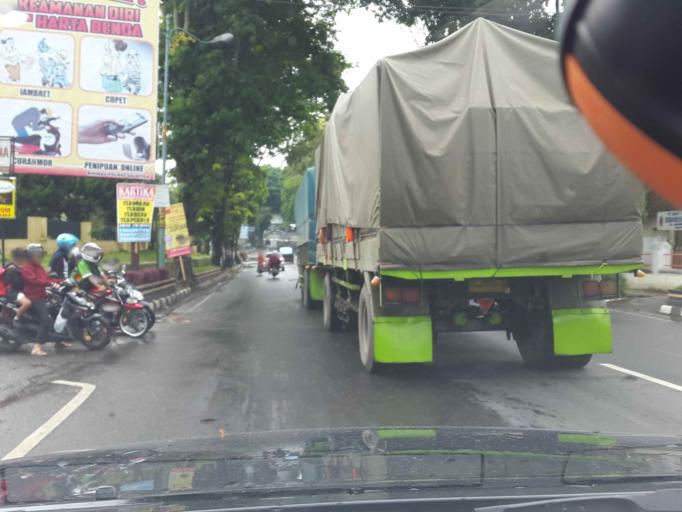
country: ID
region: Central Java
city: Salatiga
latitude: -7.3162
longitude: 110.4944
